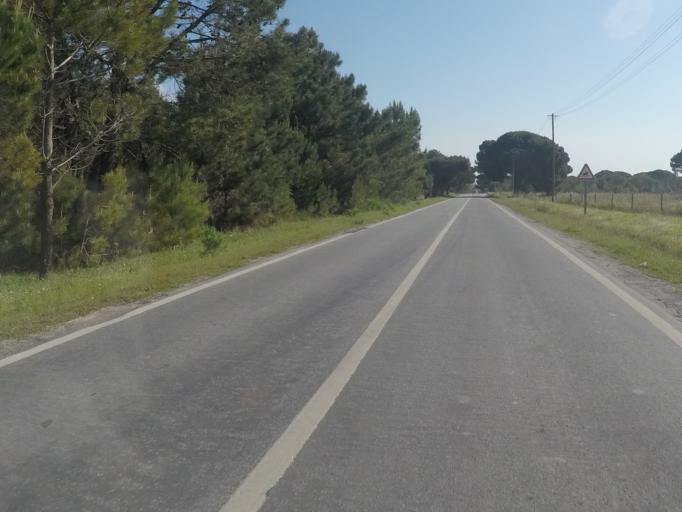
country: PT
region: Setubal
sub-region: Sesimbra
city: Sesimbra
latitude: 38.4939
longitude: -9.1557
